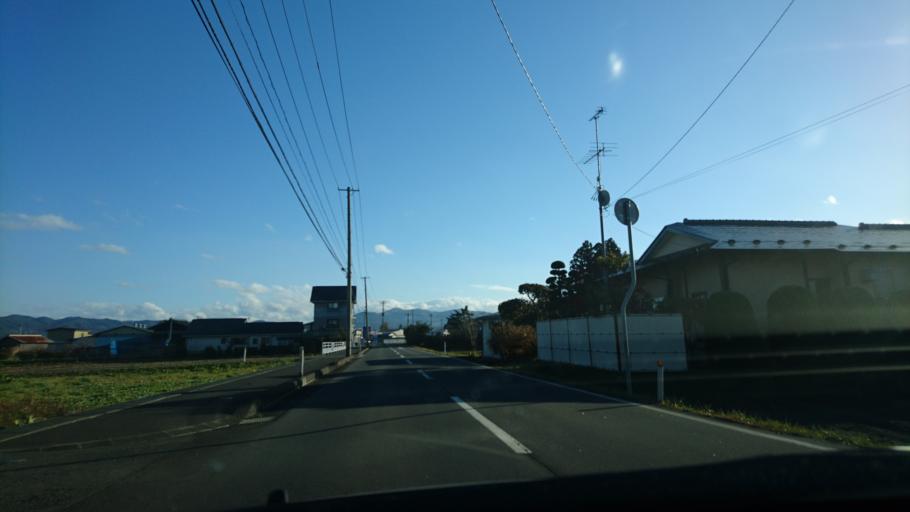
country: JP
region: Iwate
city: Mizusawa
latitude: 39.1103
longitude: 141.1558
